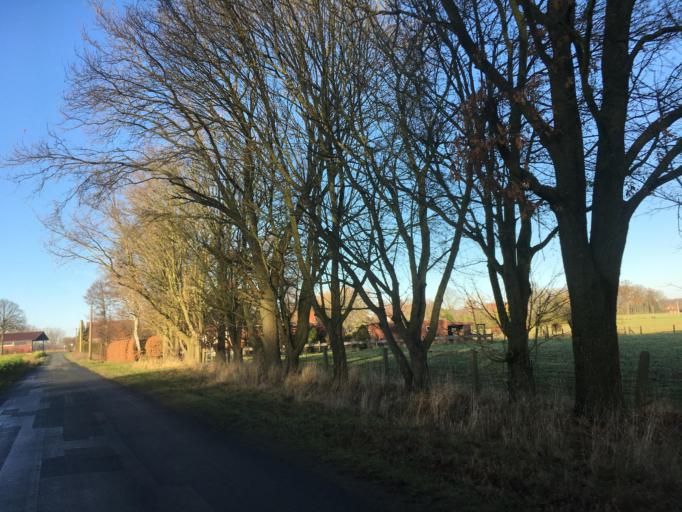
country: DE
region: North Rhine-Westphalia
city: Ludinghausen
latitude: 51.8043
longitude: 7.3702
